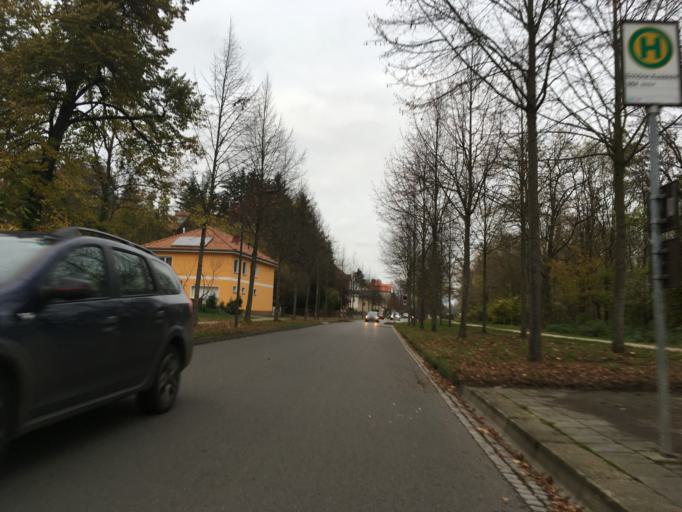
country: DE
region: Brandenburg
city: Frankfurt (Oder)
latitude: 52.3224
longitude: 14.5537
